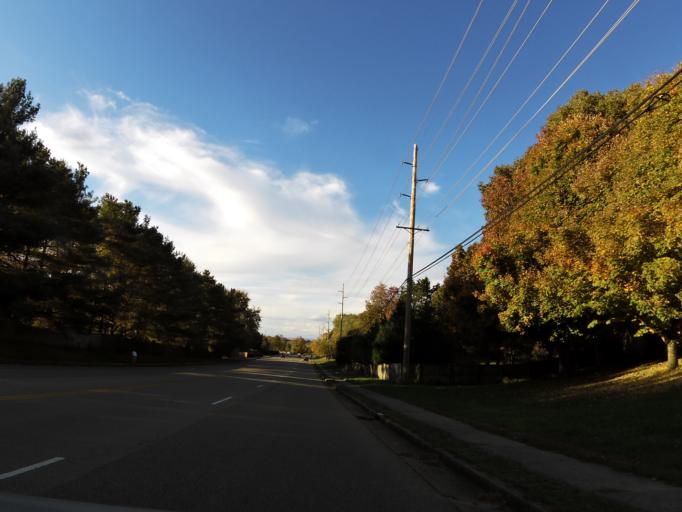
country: US
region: Tennessee
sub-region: Blount County
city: Louisville
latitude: 35.8875
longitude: -84.0653
